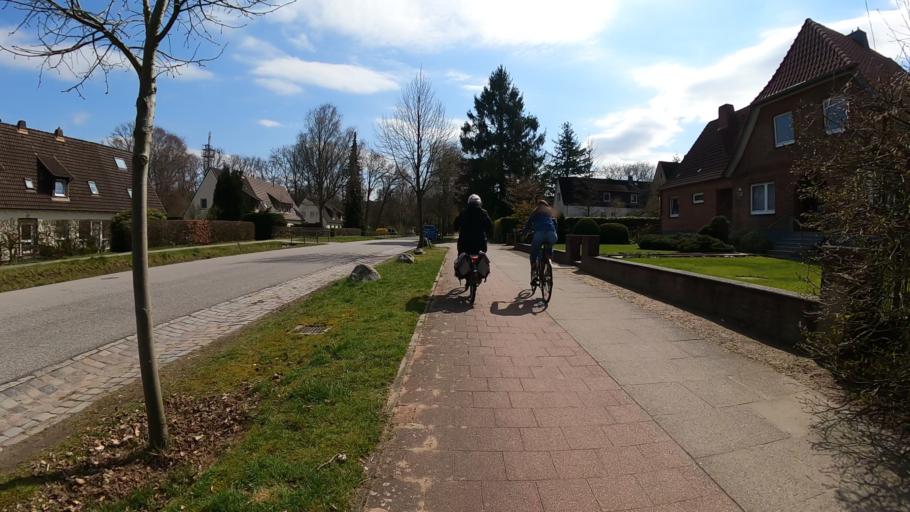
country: DE
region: Lower Saxony
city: Neu Wulmstorf
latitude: 53.4524
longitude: 9.8671
